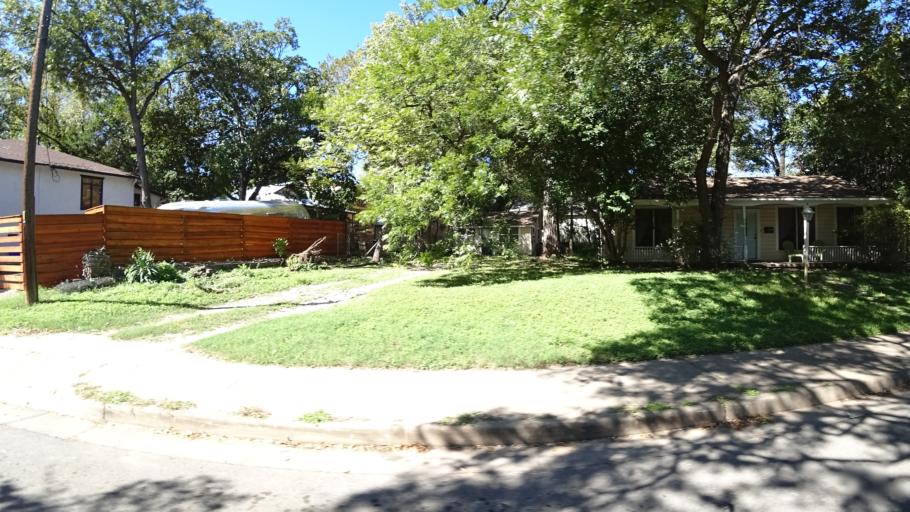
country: US
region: Texas
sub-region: Travis County
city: Austin
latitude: 30.2403
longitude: -97.7477
